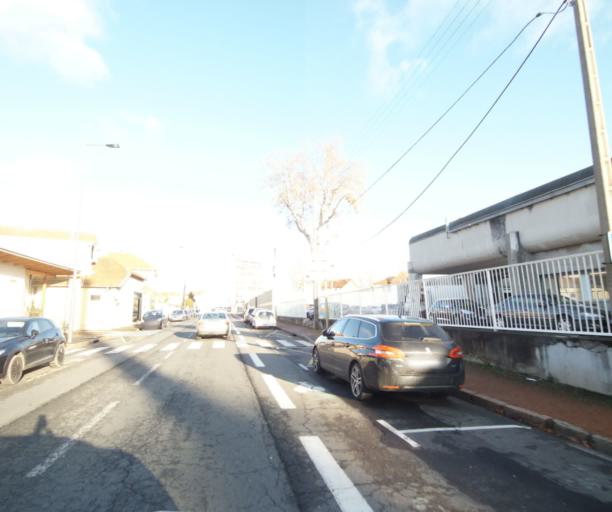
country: FR
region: Rhone-Alpes
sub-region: Departement de la Loire
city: Roanne
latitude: 46.0437
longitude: 4.0806
